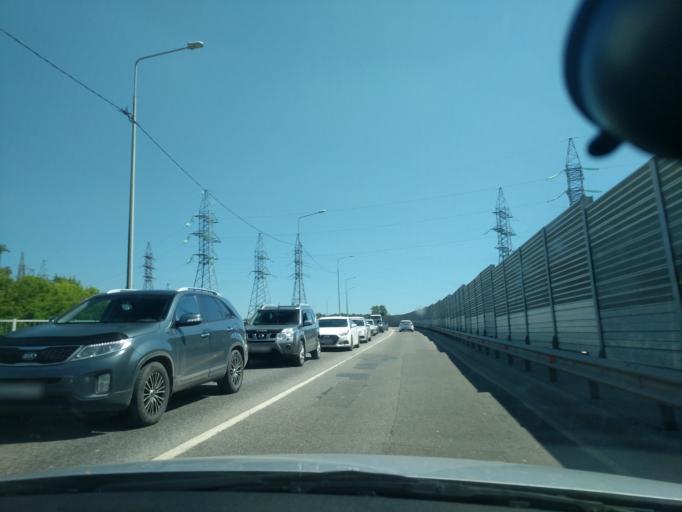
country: RU
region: Moskovskaya
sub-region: Chekhovskiy Rayon
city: Chekhov
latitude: 55.1411
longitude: 37.4839
